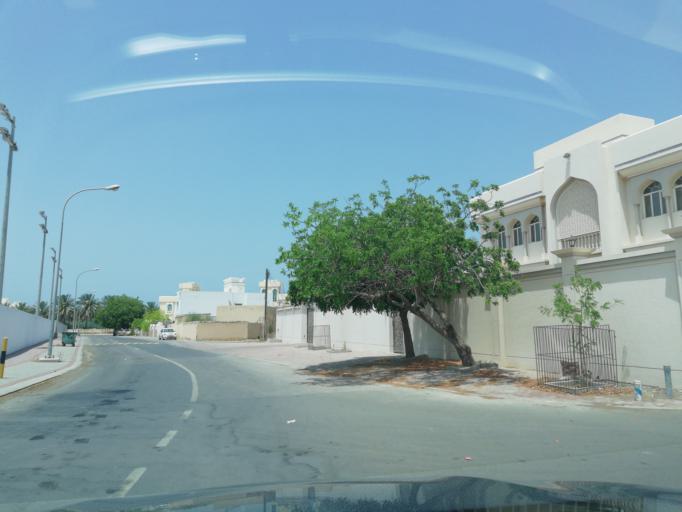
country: OM
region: Muhafazat Masqat
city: As Sib al Jadidah
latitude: 23.6607
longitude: 58.1950
